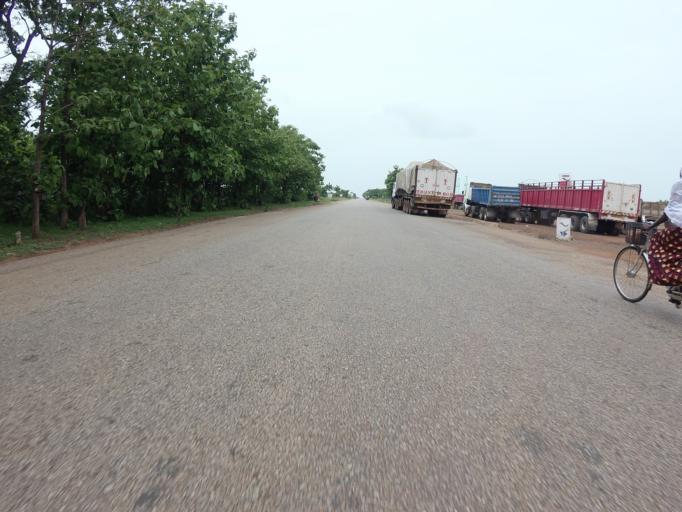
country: GH
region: Northern
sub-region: Yendi
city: Yendi
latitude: 9.4295
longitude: -0.0085
